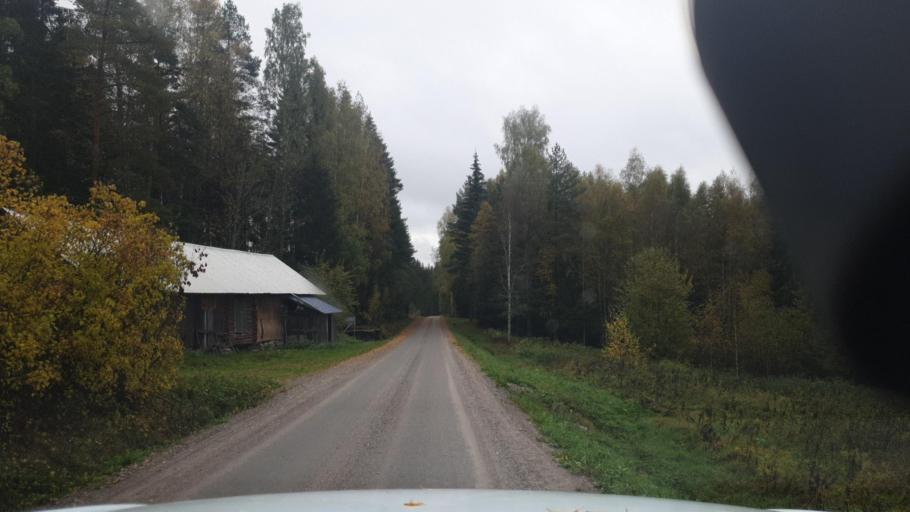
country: SE
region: Vaermland
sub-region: Karlstads Kommun
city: Edsvalla
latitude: 59.5341
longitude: 12.9946
